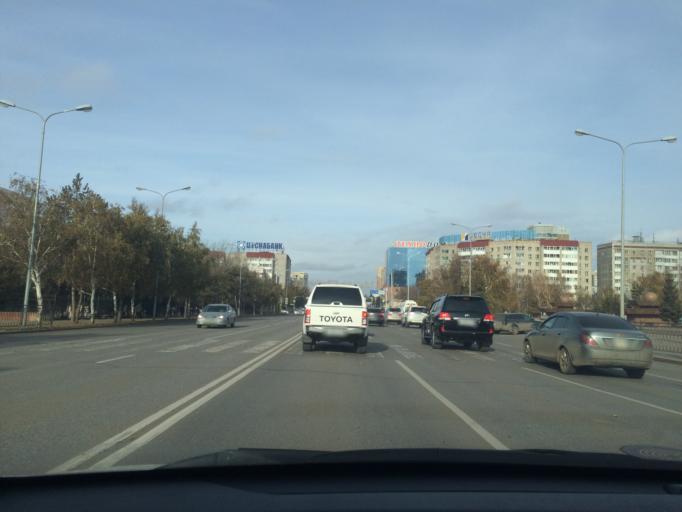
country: KZ
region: Astana Qalasy
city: Astana
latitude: 51.1697
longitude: 71.4262
